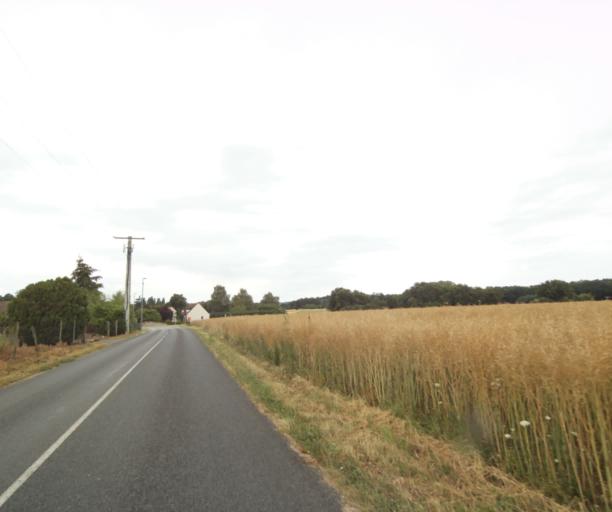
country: FR
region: Ile-de-France
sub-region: Departement de l'Essonne
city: Soisy-sur-Ecole
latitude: 48.4799
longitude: 2.5056
